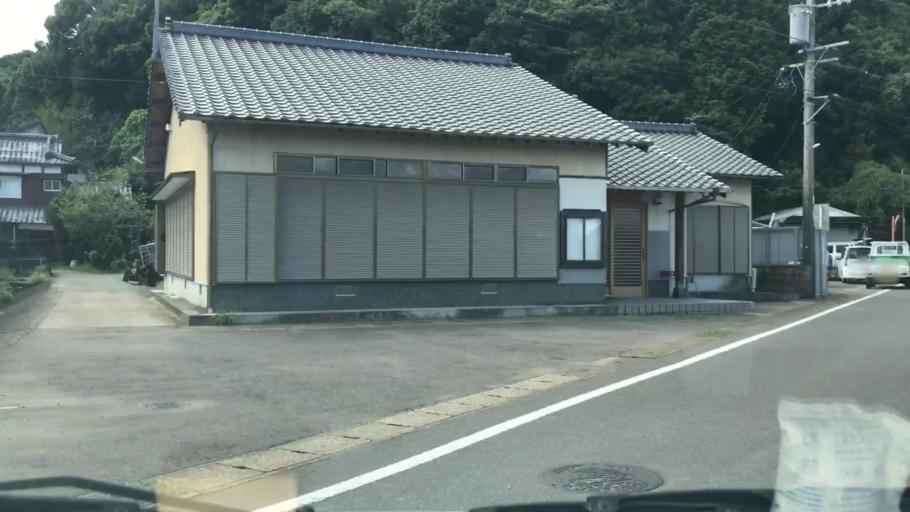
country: JP
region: Saga Prefecture
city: Kashima
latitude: 33.1178
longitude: 130.0702
